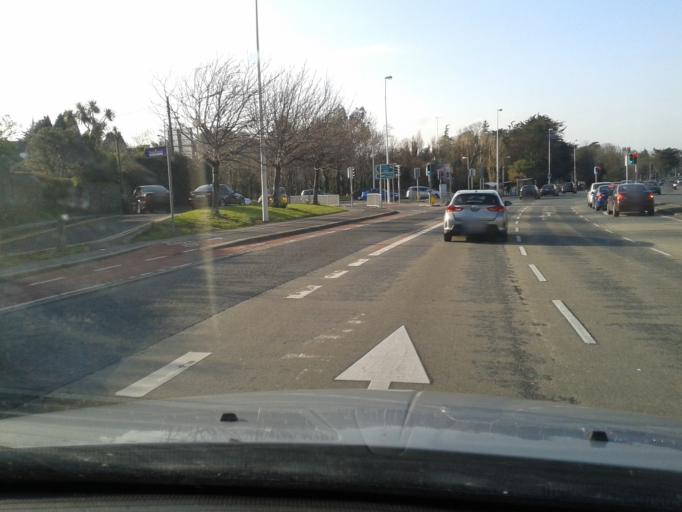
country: IE
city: Booterstown
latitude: 53.2817
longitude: -6.1930
